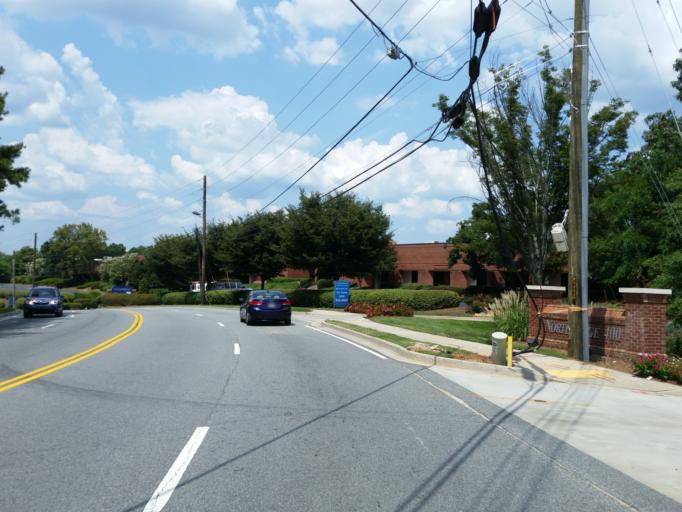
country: US
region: Georgia
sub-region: Fulton County
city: Roswell
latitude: 33.9879
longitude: -84.3413
